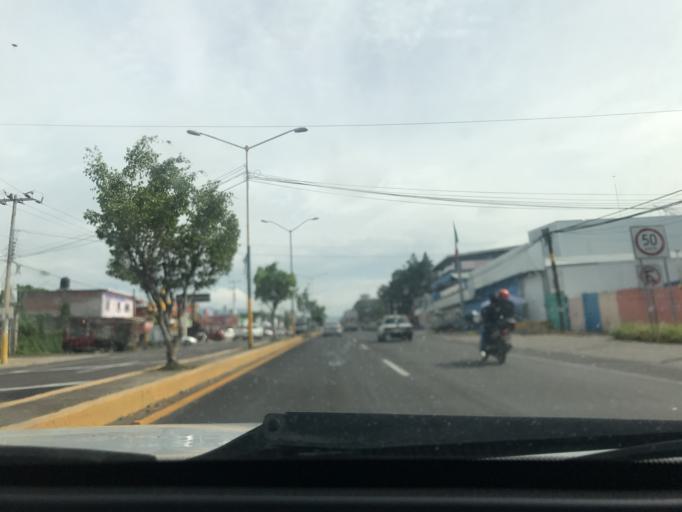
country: MX
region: Morelos
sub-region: Cuautla
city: Tierra Larga (Campo Nuevo)
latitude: 18.8735
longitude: -98.9246
